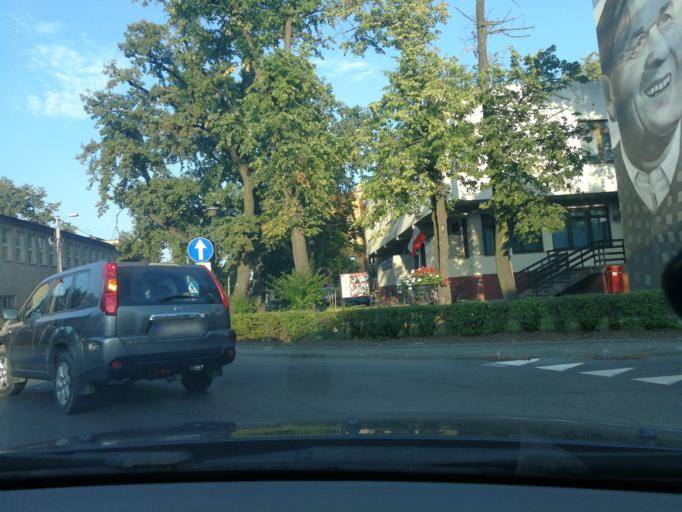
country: PL
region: Masovian Voivodeship
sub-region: Powiat pruszkowski
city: Brwinow
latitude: 52.1403
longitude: 20.7182
